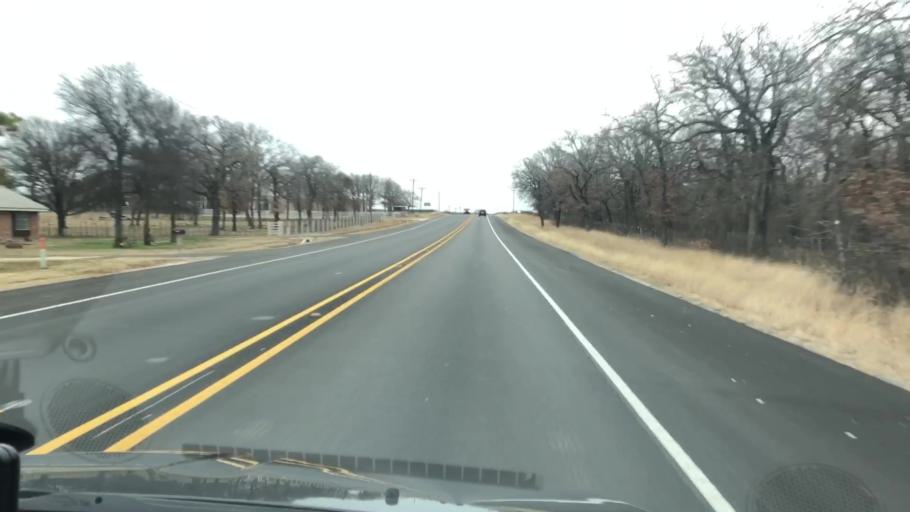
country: US
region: Texas
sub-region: Erath County
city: Stephenville
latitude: 32.4198
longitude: -98.1512
